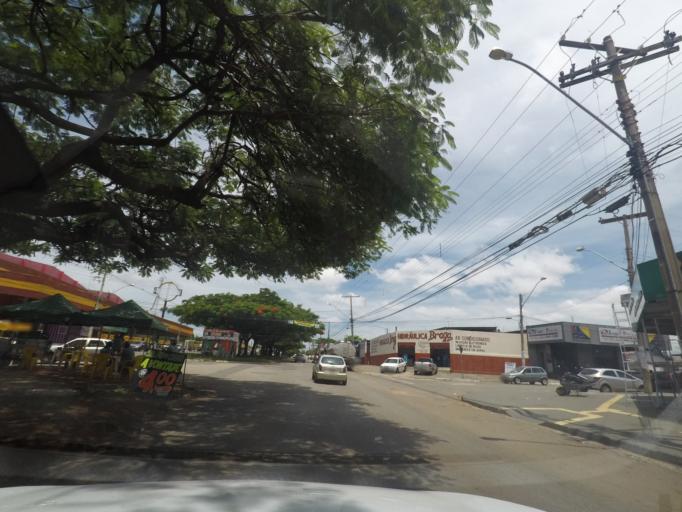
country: BR
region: Goias
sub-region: Goiania
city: Goiania
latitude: -16.6626
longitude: -49.2131
